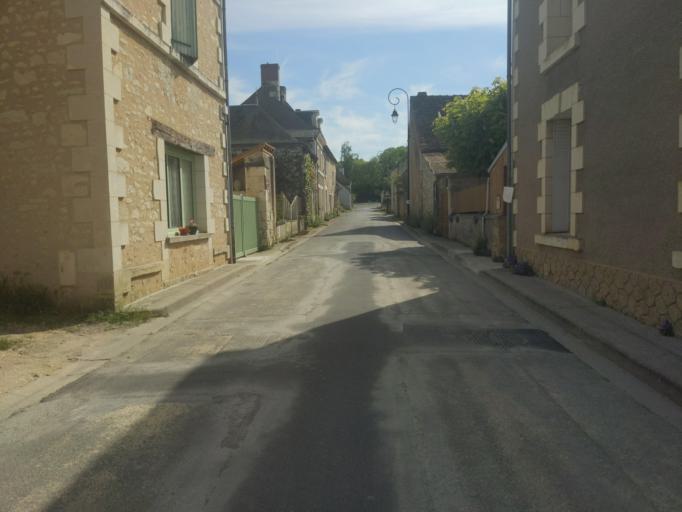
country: FR
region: Centre
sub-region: Departement d'Indre-et-Loire
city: Preuilly-sur-Claise
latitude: 46.8705
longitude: 0.8619
